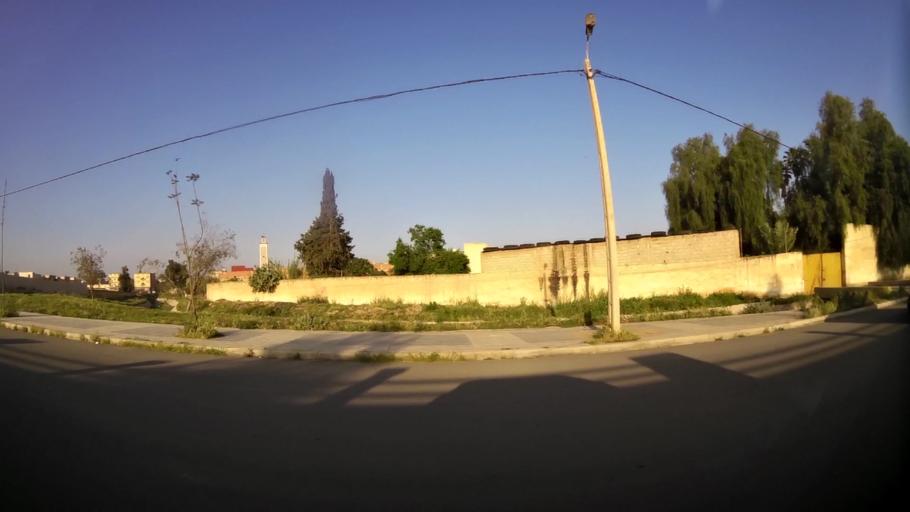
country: MA
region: Oriental
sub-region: Oujda-Angad
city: Oujda
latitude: 34.6728
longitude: -1.9365
